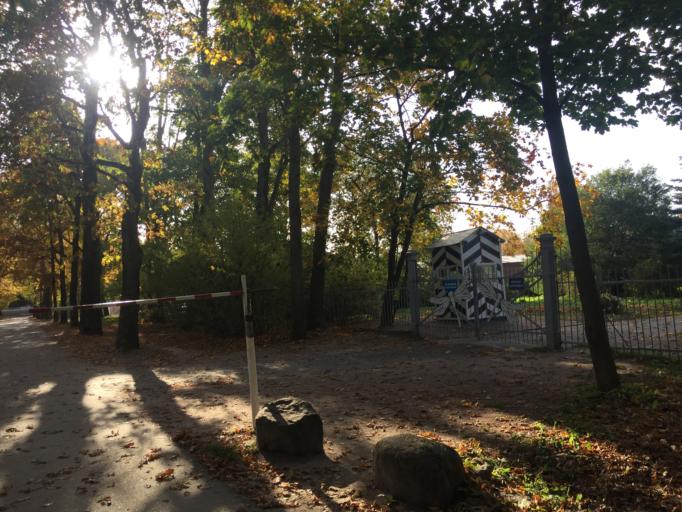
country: RU
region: St.-Petersburg
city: Pushkin
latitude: 59.7157
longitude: 30.3856
